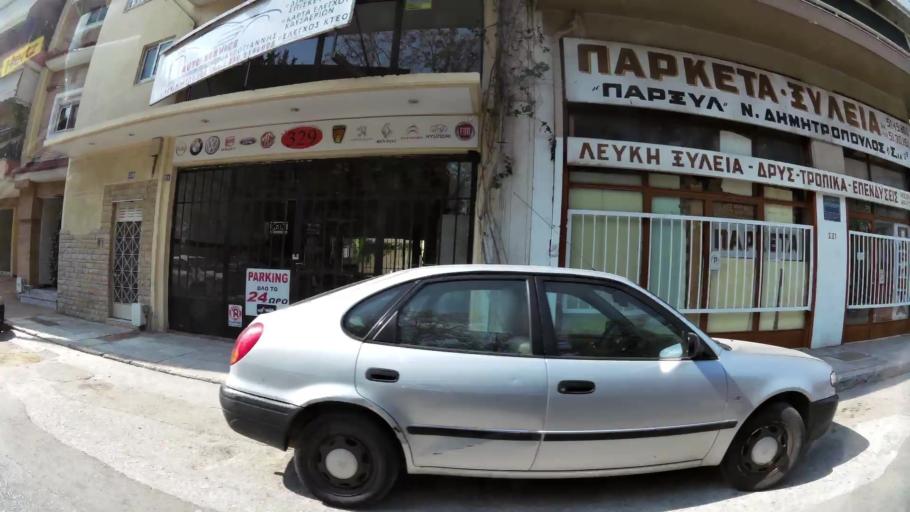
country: GR
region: Attica
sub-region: Nomarchia Athinas
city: Kipseli
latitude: 37.9987
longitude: 23.7202
